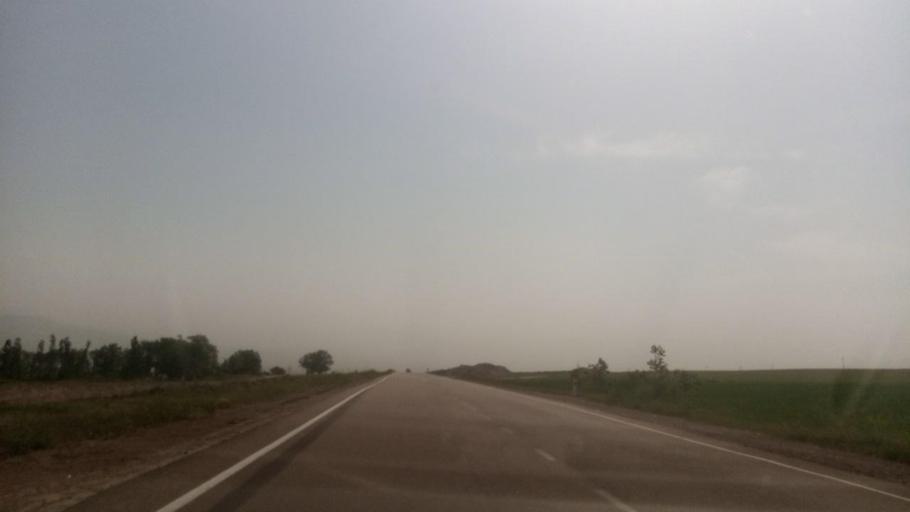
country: UZ
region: Toshkent
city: Angren
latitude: 41.0426
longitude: 70.1495
